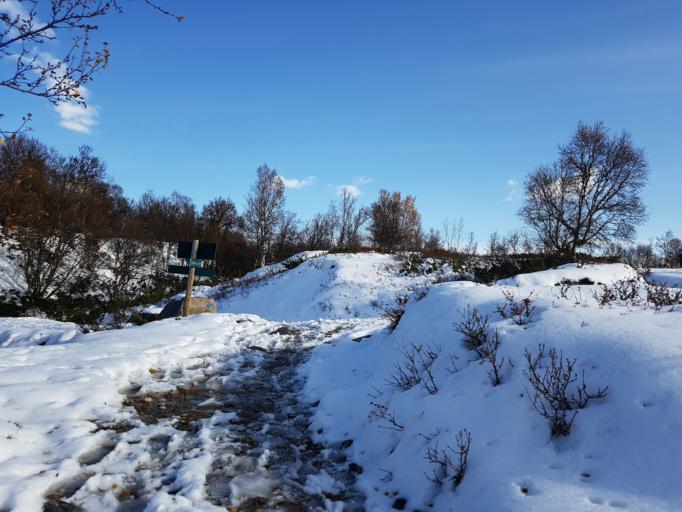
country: NO
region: Oppland
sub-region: Sel
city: Otta
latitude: 61.8282
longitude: 9.6954
